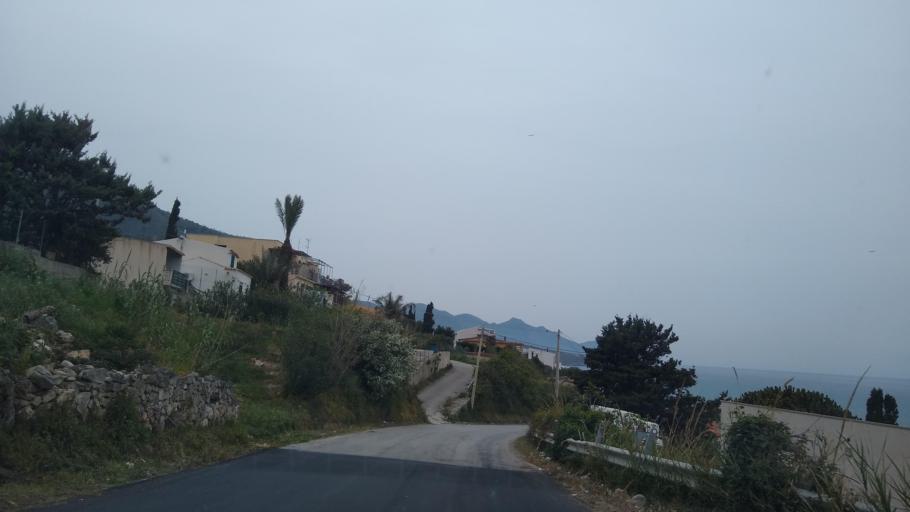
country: IT
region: Sicily
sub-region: Trapani
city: Castellammare del Golfo
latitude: 38.0204
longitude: 12.8980
